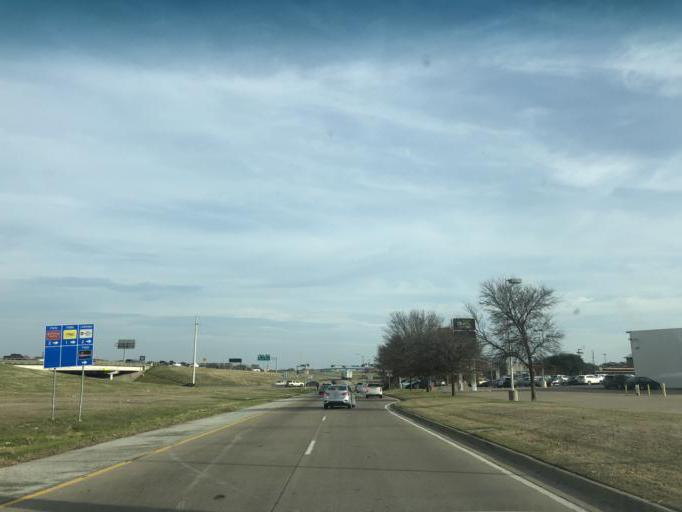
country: US
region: Texas
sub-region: Dallas County
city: Duncanville
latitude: 32.6598
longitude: -96.8930
